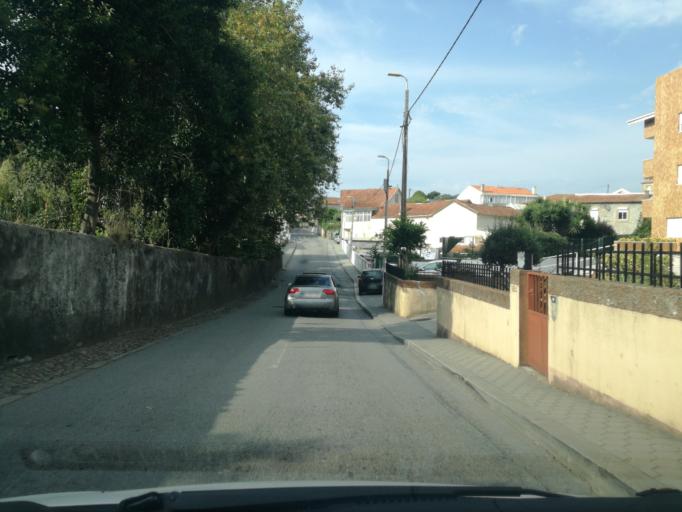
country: PT
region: Porto
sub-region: Vila Nova de Gaia
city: Azenha
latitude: 41.0765
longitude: -8.6249
